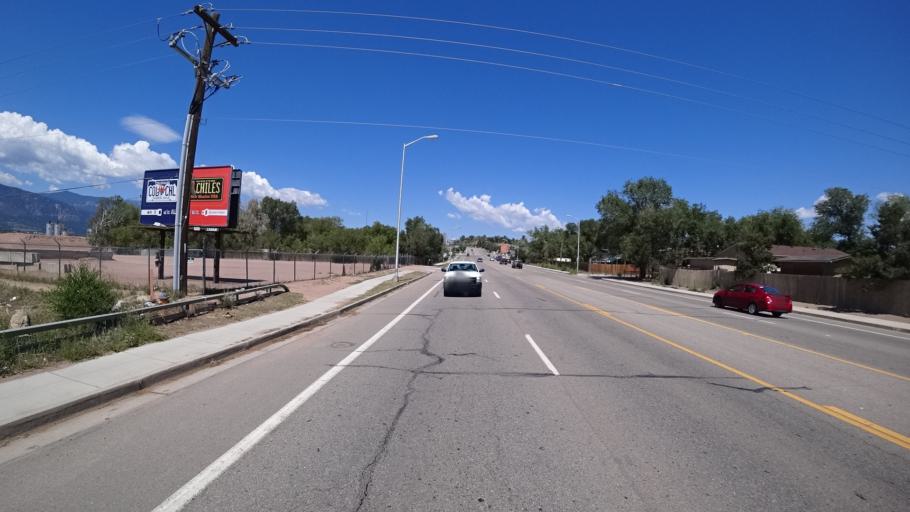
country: US
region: Colorado
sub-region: El Paso County
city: Stratmoor
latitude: 38.7927
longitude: -104.7659
